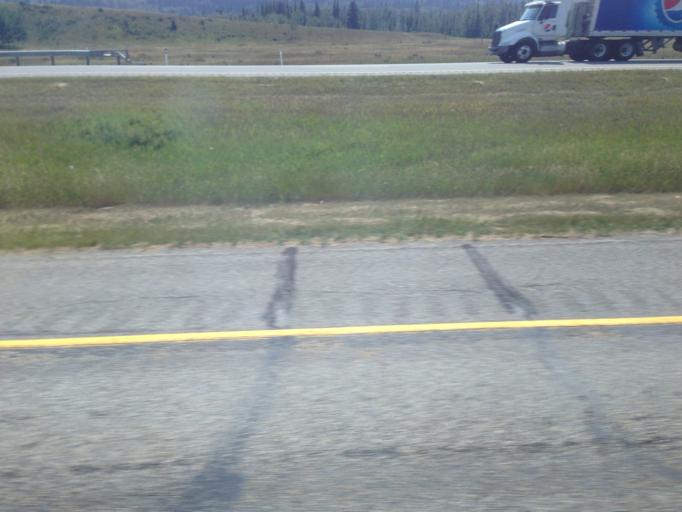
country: CA
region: Alberta
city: Canmore
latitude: 51.1344
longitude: -114.9240
